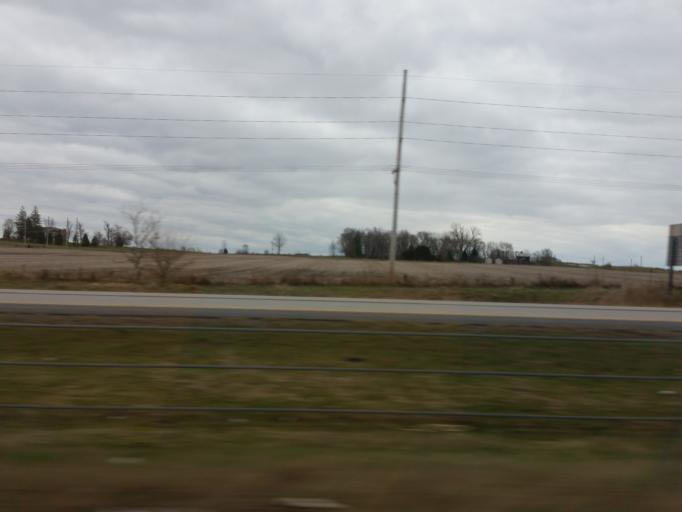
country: US
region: Iowa
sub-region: Johnson County
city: Tiffin
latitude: 41.7292
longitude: -91.6424
